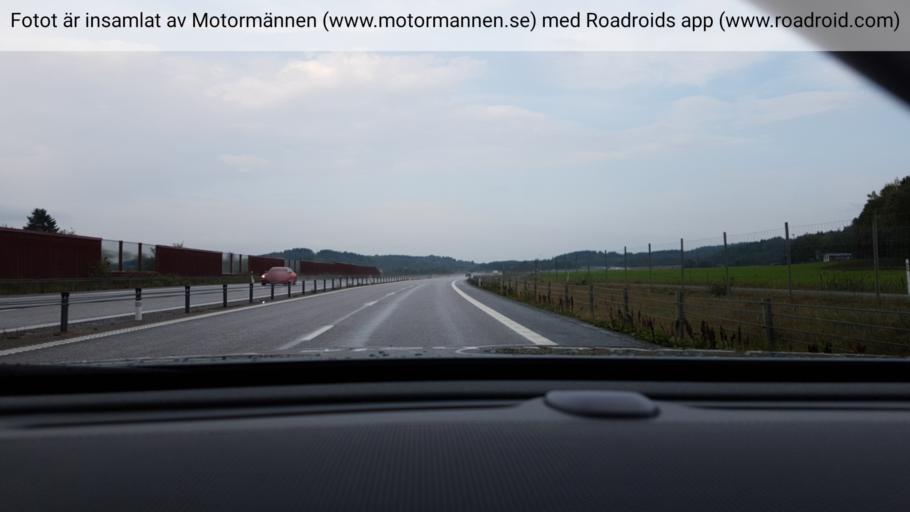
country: SE
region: Vaestra Goetaland
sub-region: Lilla Edets Kommun
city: Lodose
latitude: 58.0058
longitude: 12.1612
